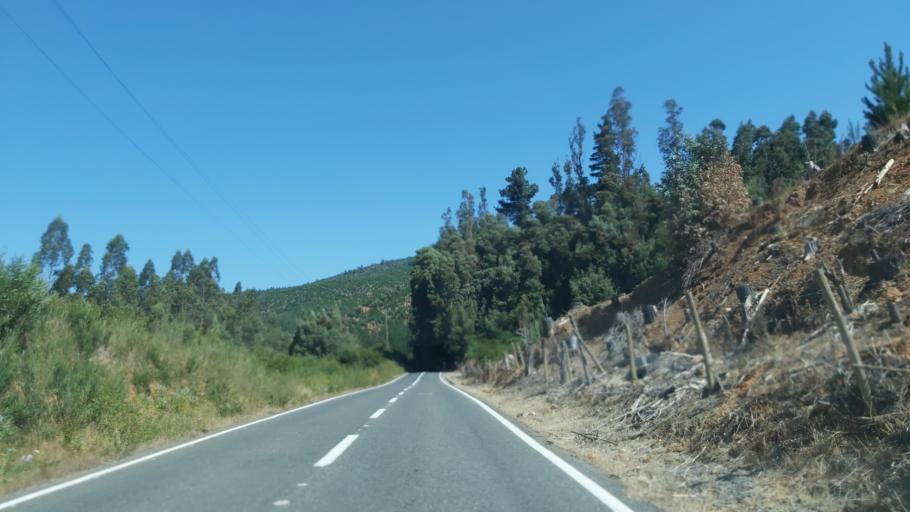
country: CL
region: Biobio
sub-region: Provincia de Concepcion
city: Tome
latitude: -36.5505
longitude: -72.8789
